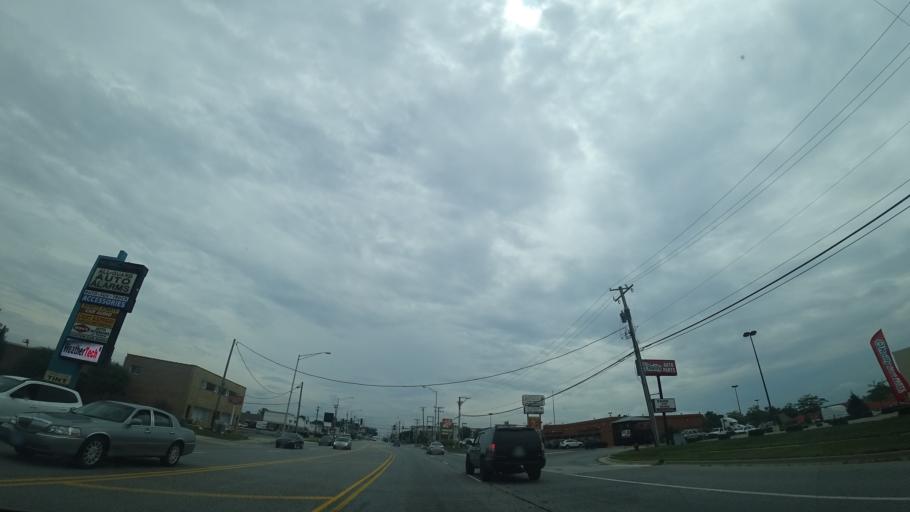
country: US
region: Illinois
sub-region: Cook County
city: Alsip
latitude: 41.6756
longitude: -87.7391
